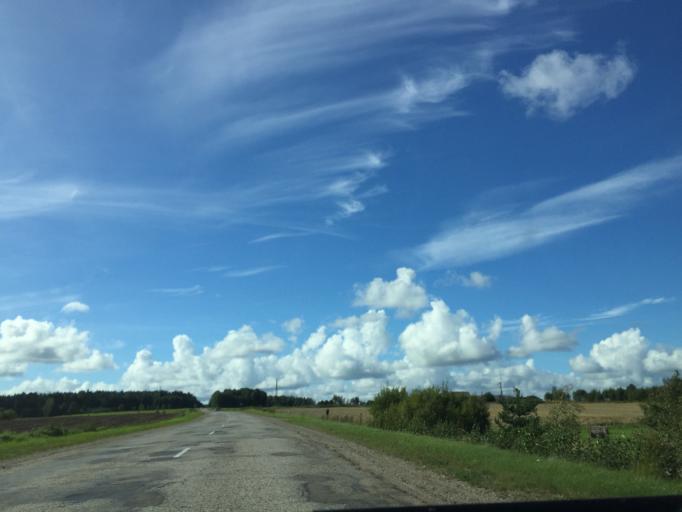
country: LV
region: Kuldigas Rajons
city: Kuldiga
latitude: 56.9868
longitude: 21.7960
